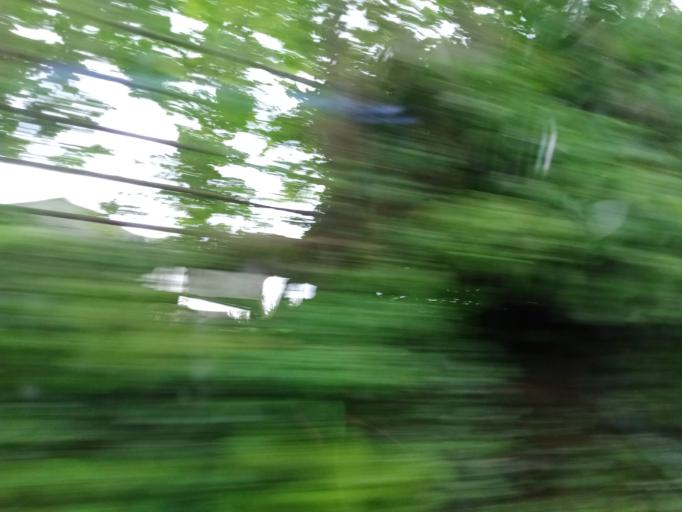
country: IE
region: Munster
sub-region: County Cork
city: Bandon
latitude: 51.7263
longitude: -8.7748
